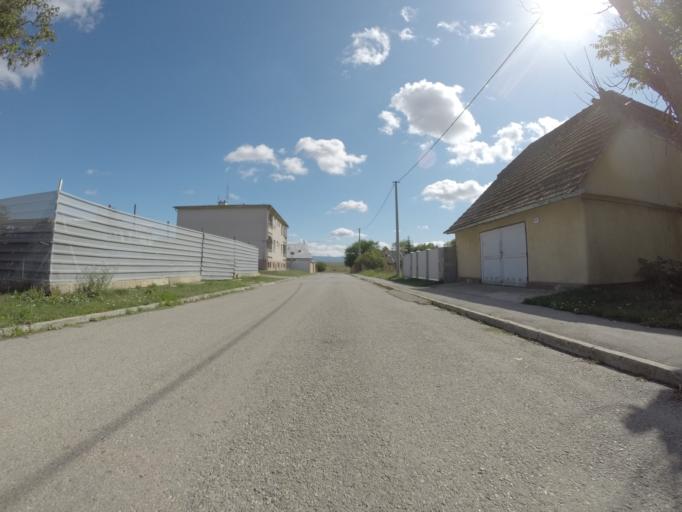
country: SK
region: Trenciansky
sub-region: Okres Nove Mesto nad Vahom
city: Nove Mesto nad Vahom
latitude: 48.7882
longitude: 17.7775
